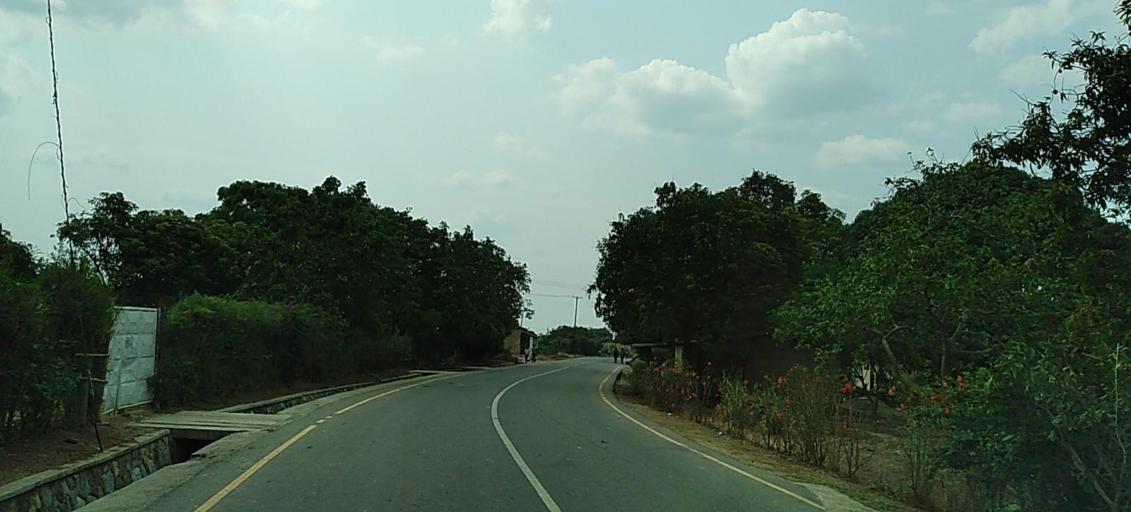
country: ZM
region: Copperbelt
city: Kalulushi
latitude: -12.8537
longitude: 28.1294
